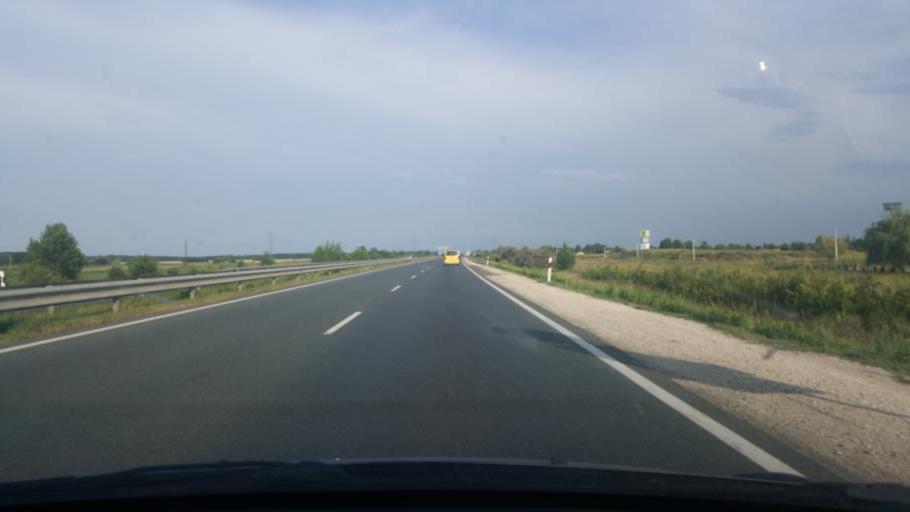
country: HU
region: Pest
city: Ullo
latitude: 47.4008
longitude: 19.3545
